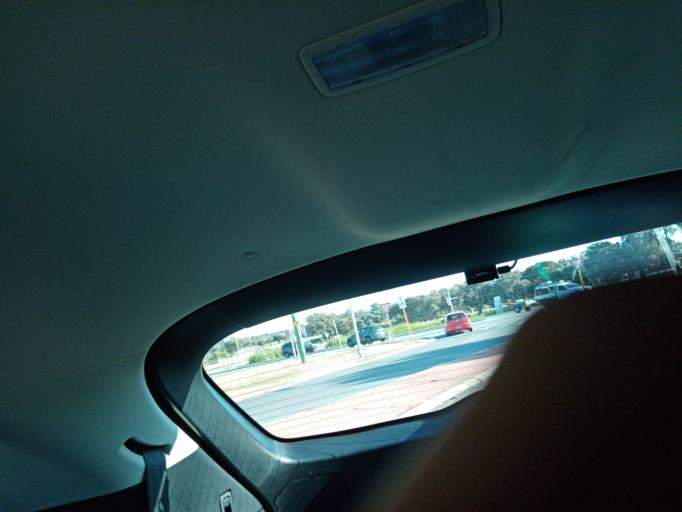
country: AU
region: Western Australia
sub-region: City of Cockburn
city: South Lake
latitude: -32.1180
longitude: 115.8404
